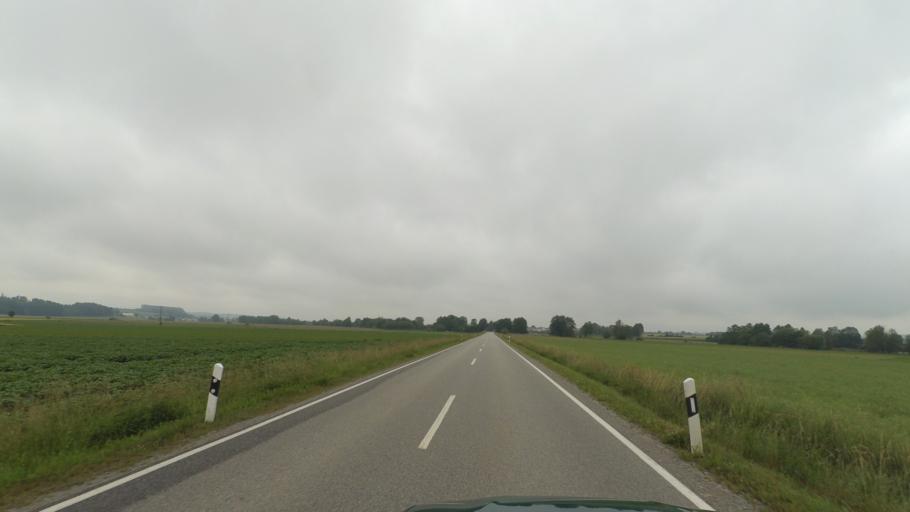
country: DE
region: Bavaria
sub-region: Lower Bavaria
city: Laberweinting
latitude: 48.7921
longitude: 12.2959
